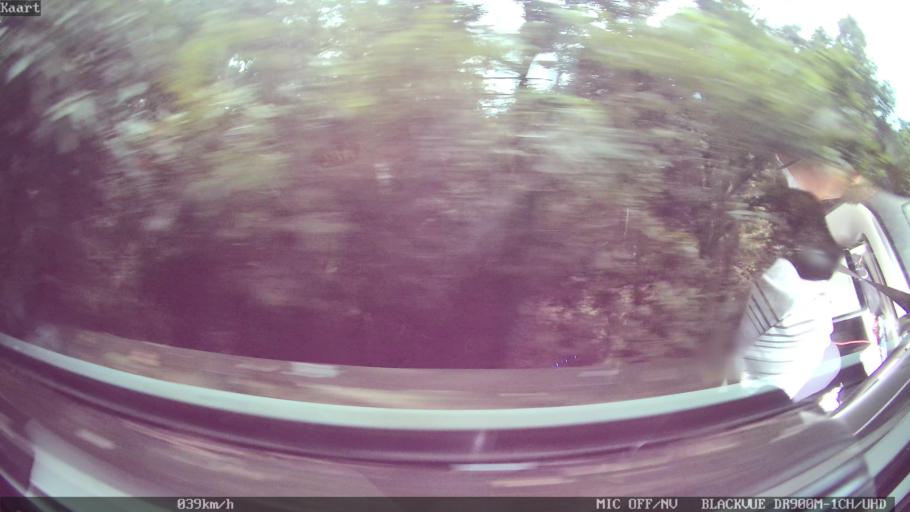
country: ID
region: Bali
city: Petang
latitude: -8.3817
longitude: 115.2221
